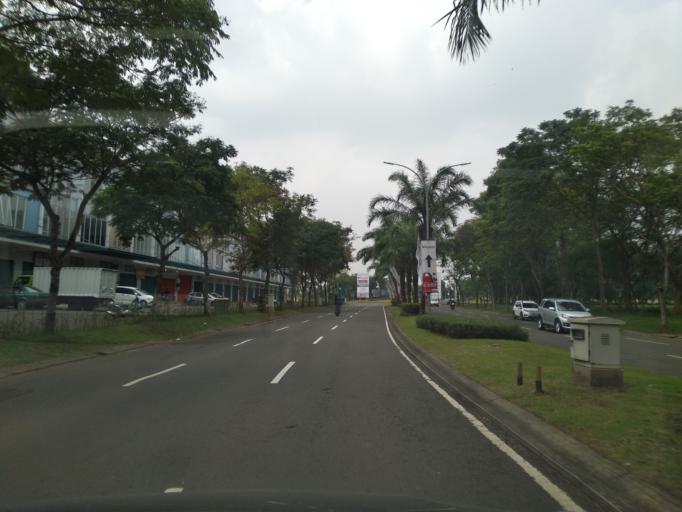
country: ID
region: West Java
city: Bekasi
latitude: -6.2908
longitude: 107.0447
